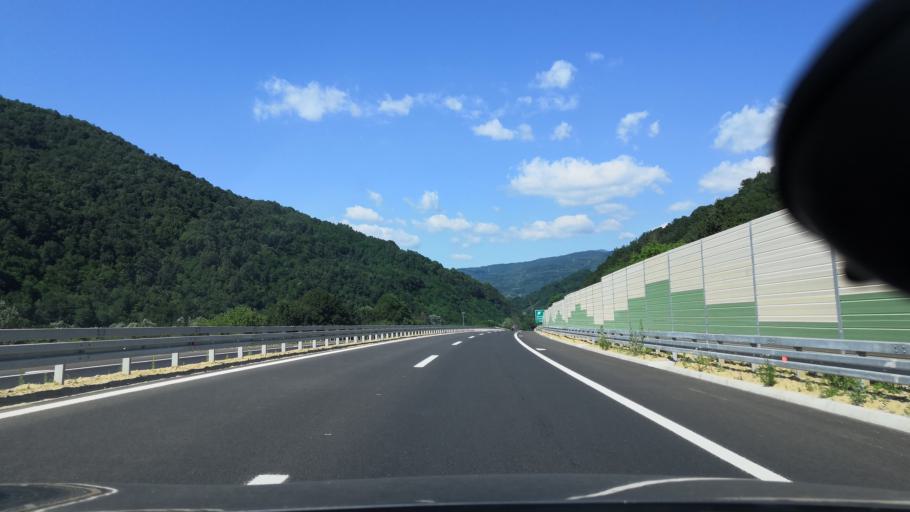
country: RS
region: Central Serbia
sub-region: Pcinjski Okrug
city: Vladicin Han
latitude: 42.8031
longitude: 22.1049
